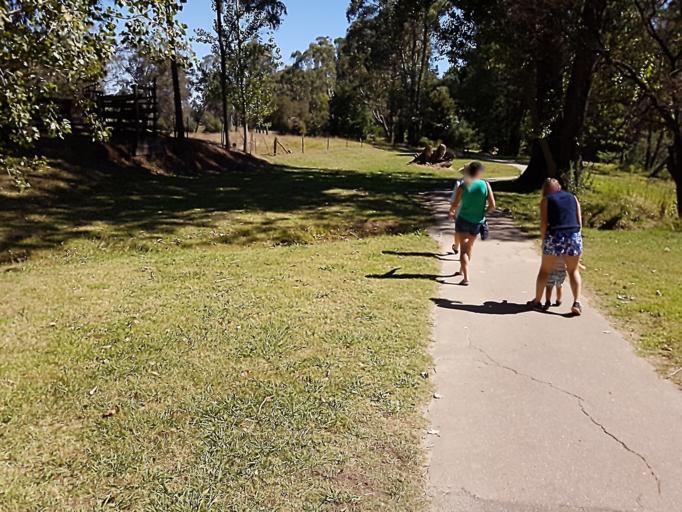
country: AU
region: Victoria
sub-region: Alpine
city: Mount Beauty
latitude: -36.7278
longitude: 146.9532
